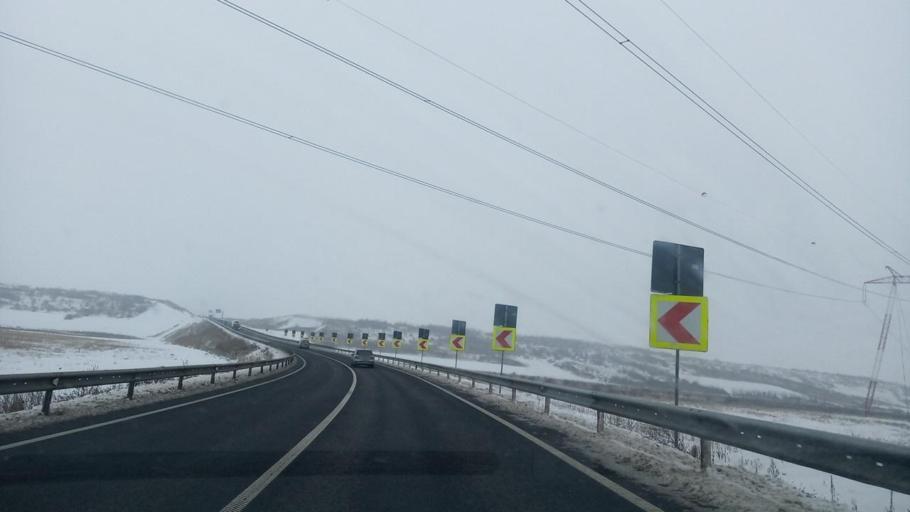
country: RO
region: Bacau
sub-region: Comuna Saucesti
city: Saucesti
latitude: 46.6384
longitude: 26.9285
